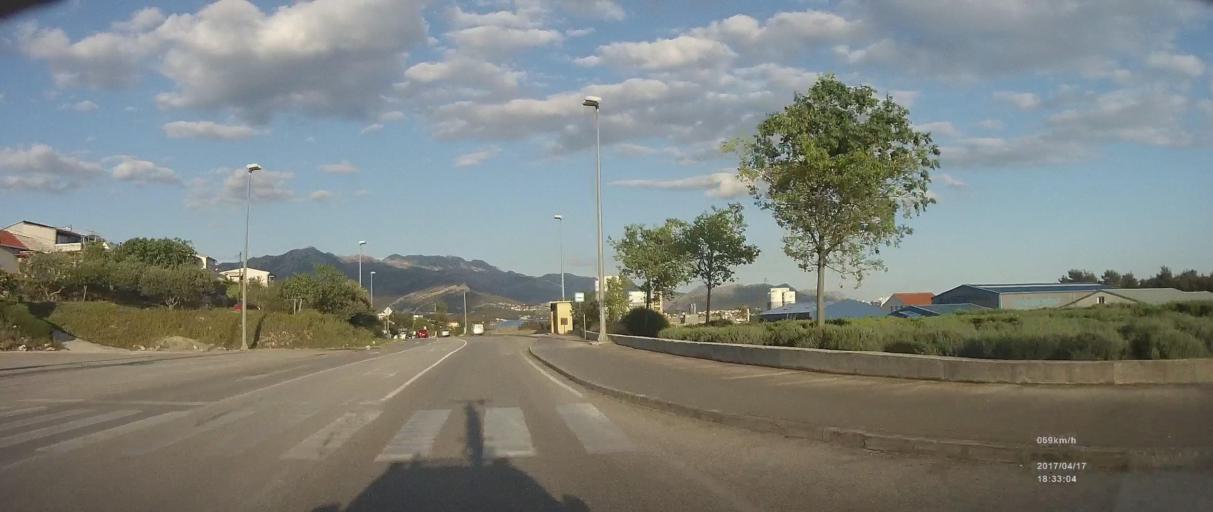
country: HR
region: Splitsko-Dalmatinska
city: Vranjic
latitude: 43.5411
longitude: 16.4545
